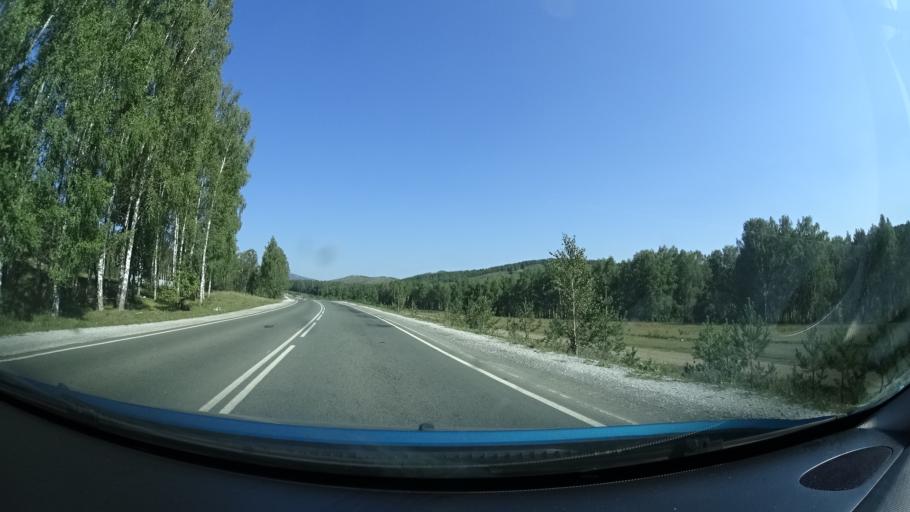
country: RU
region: Bashkortostan
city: Abzakovo
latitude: 53.8449
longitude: 58.5826
